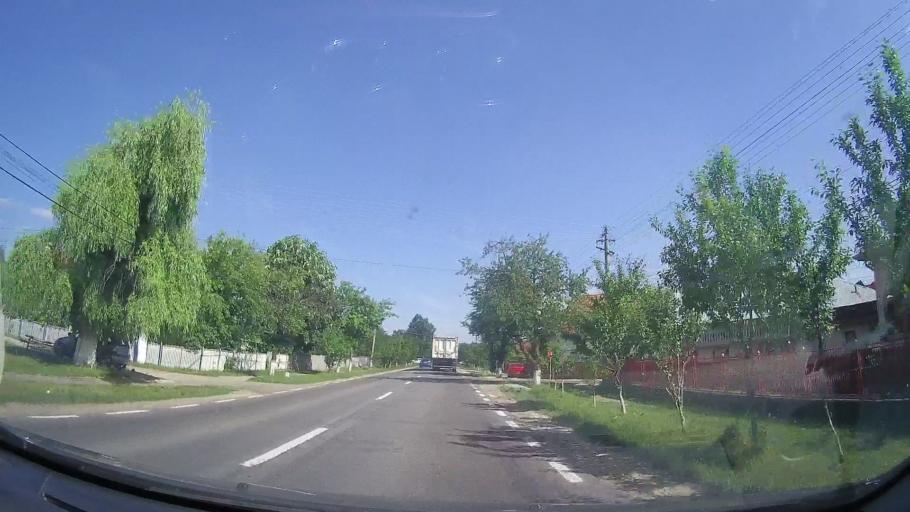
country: RO
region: Prahova
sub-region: Comuna Izvoarele
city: Homoraciu
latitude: 45.2565
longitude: 26.0204
